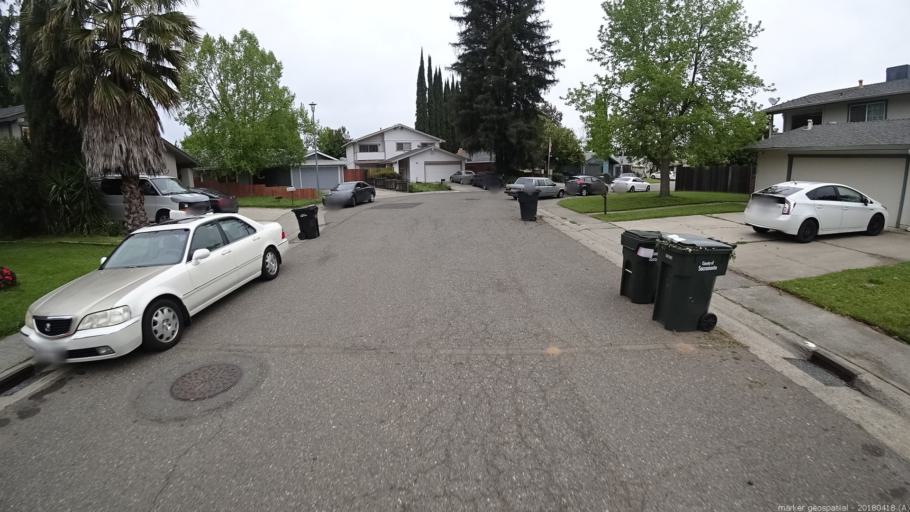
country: US
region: California
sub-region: Sacramento County
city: La Riviera
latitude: 38.5716
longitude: -121.3484
